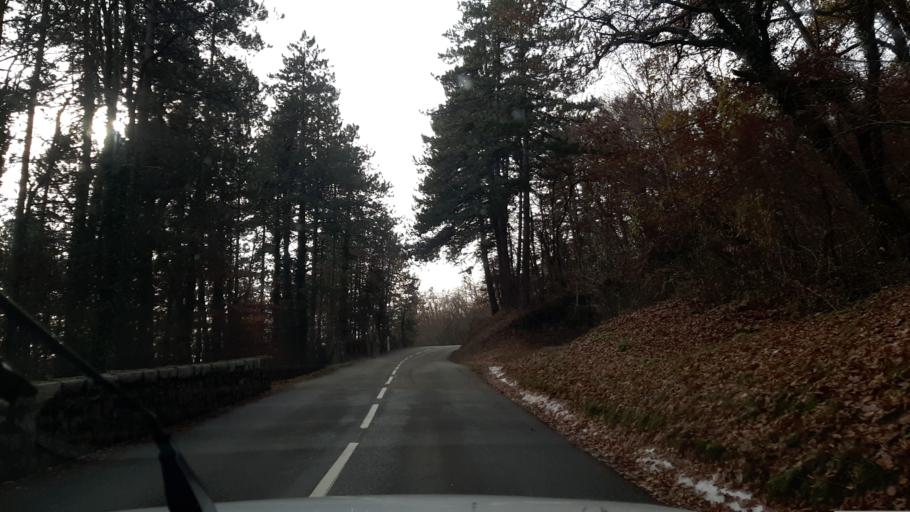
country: FR
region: Rhone-Alpes
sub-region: Departement de la Savoie
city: Coise-Saint-Jean-Pied-Gauthier
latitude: 45.5848
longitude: 6.1513
